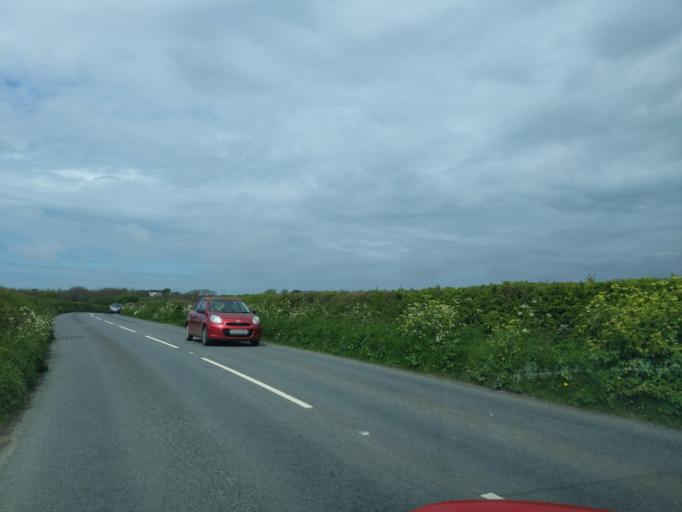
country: GB
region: England
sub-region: Cornwall
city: Wadebridge
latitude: 50.5541
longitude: -4.8642
